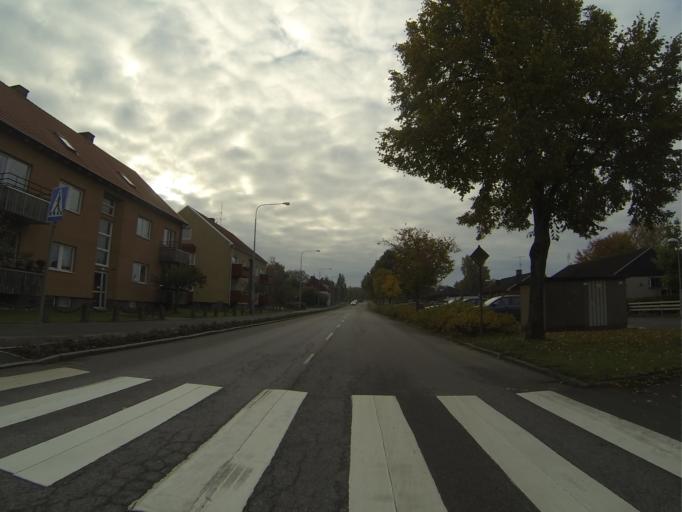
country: SE
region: Skane
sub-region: Tomelilla Kommun
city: Tomelilla
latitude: 55.5434
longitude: 13.9432
